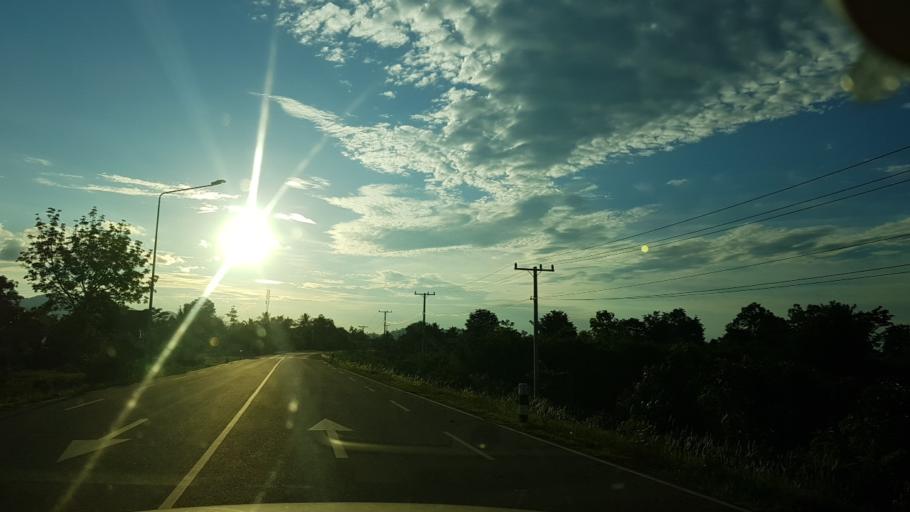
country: TH
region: Nong Khai
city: Sangkhom
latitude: 18.0918
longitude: 102.2899
